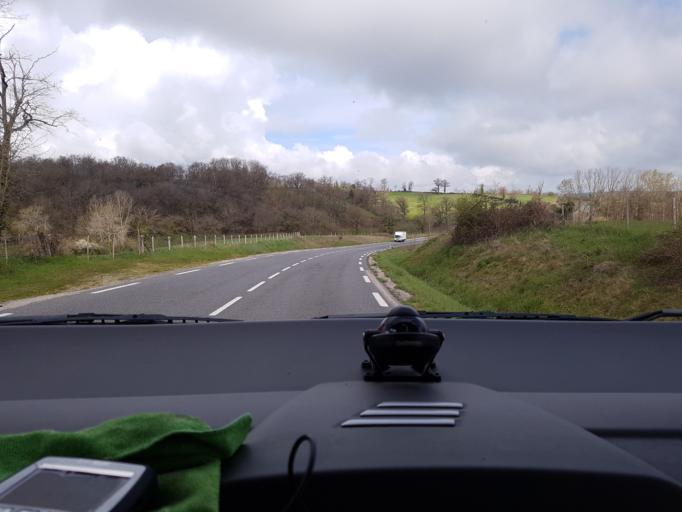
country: FR
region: Midi-Pyrenees
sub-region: Departement de l'Aveyron
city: Moyrazes
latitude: 44.3735
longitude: 2.4601
